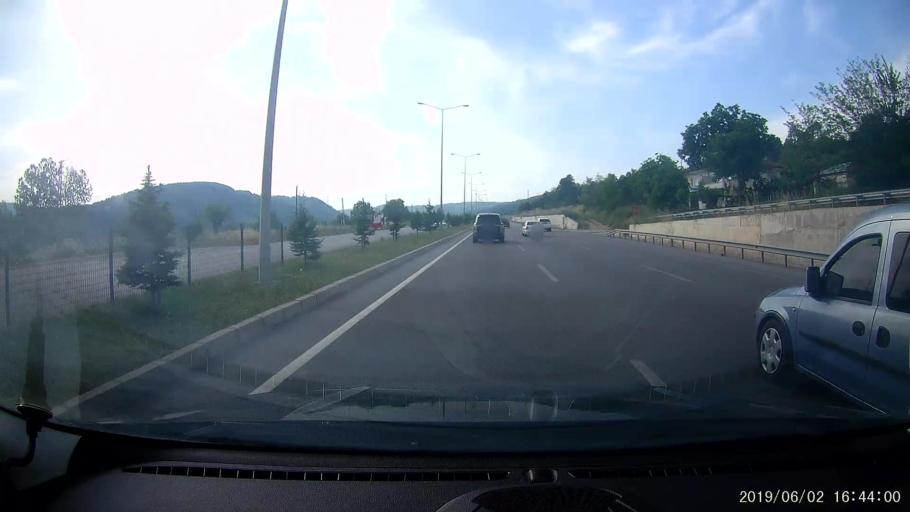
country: TR
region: Samsun
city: Kavak
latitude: 41.1440
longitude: 36.1170
